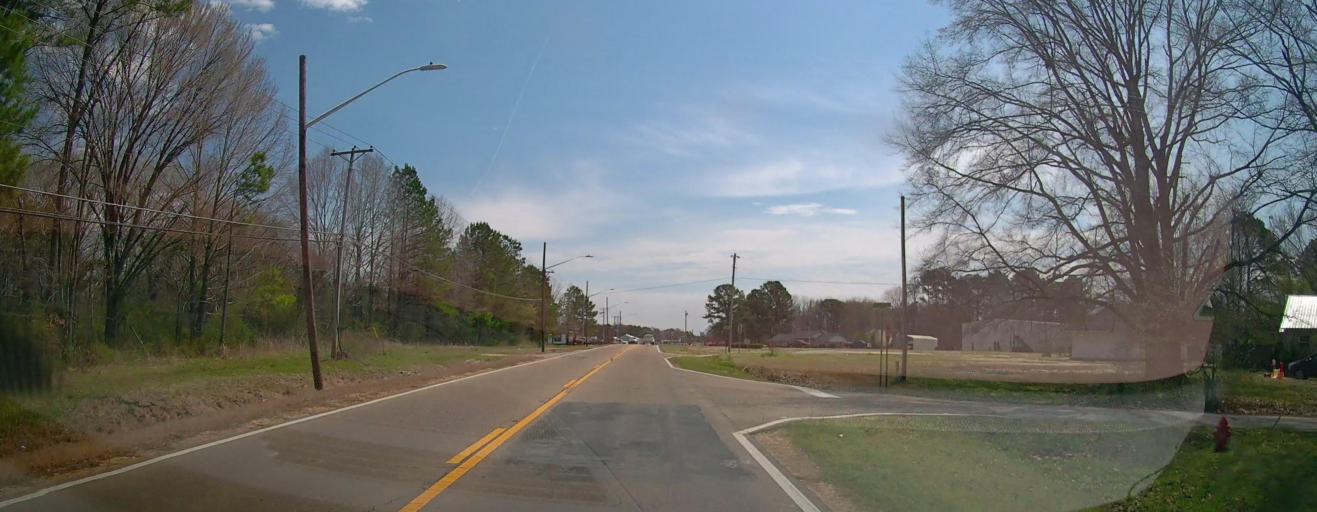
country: US
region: Mississippi
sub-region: Union County
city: New Albany
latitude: 34.5131
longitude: -89.0402
